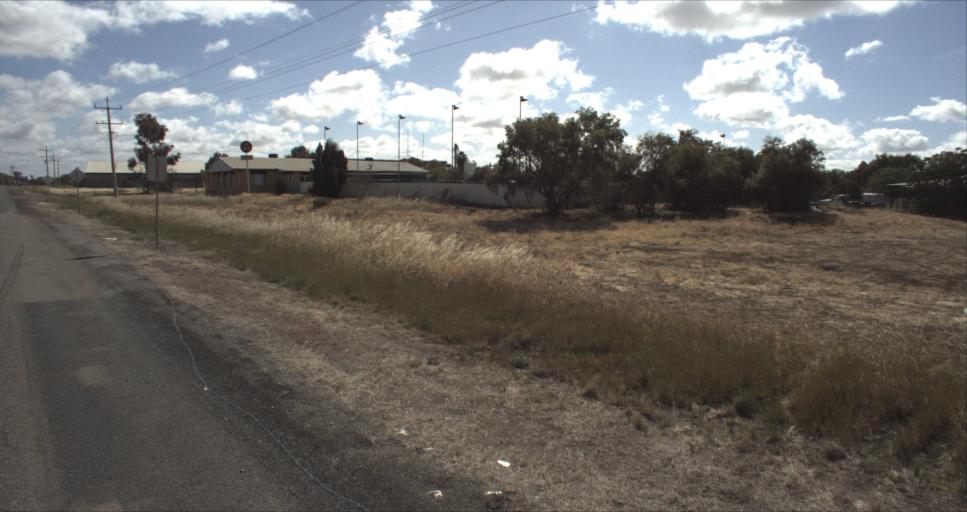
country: AU
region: New South Wales
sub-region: Murrumbidgee Shire
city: Darlington Point
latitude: -34.5167
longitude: 146.1765
